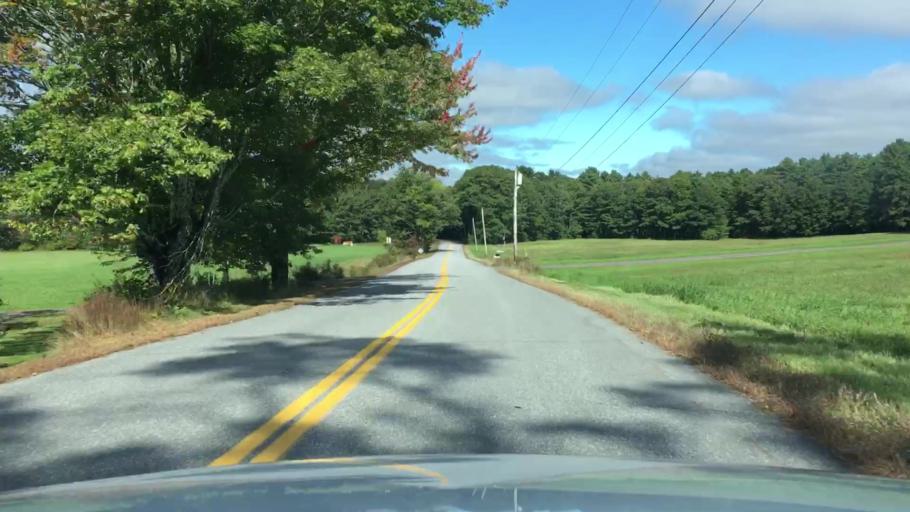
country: US
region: Maine
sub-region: Cumberland County
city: Brunswick
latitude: 43.9497
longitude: -69.8941
